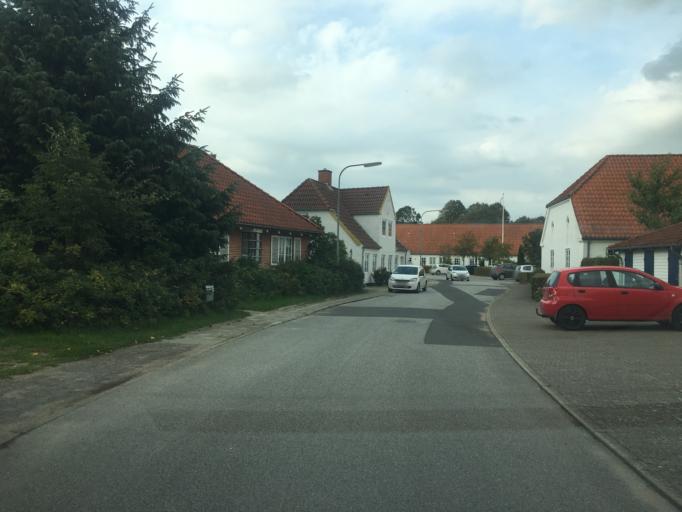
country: DK
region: South Denmark
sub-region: Tonder Kommune
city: Logumkloster
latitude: 55.0574
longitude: 8.9545
